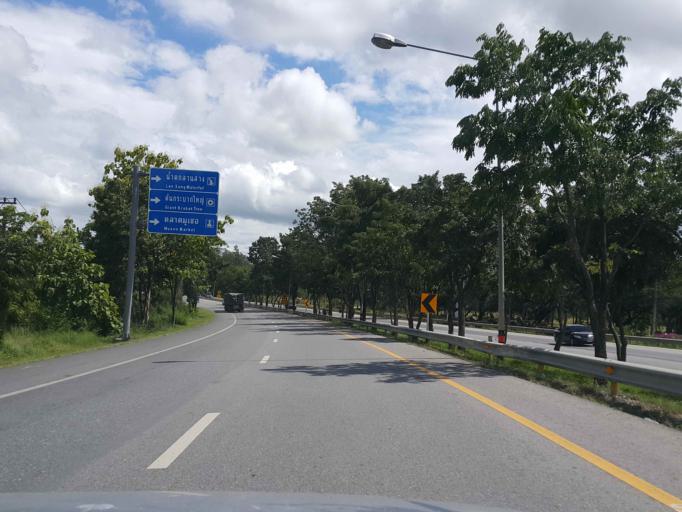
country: TH
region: Tak
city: Tak
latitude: 16.8467
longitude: 99.1117
